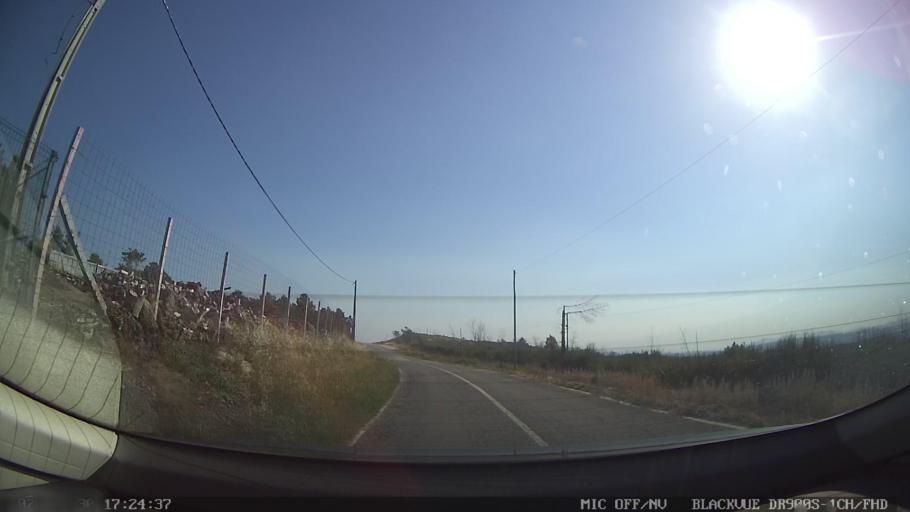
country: PT
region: Vila Real
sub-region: Murca
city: Murca
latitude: 41.3136
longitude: -7.4701
